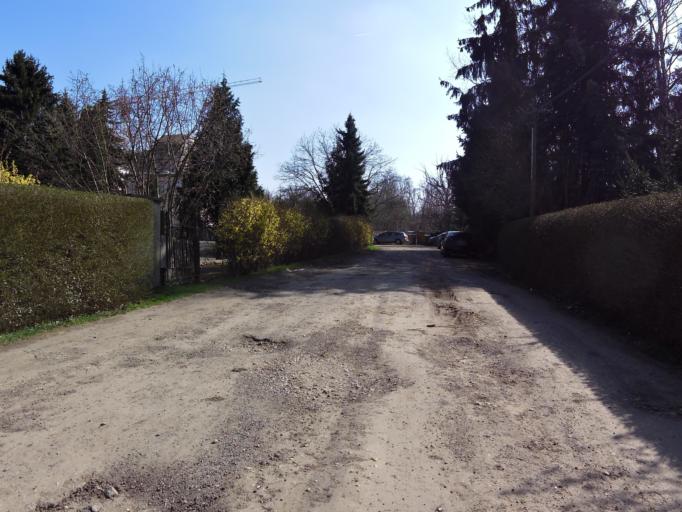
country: DE
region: Saxony
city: Schkeuditz
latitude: 51.3773
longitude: 12.2991
